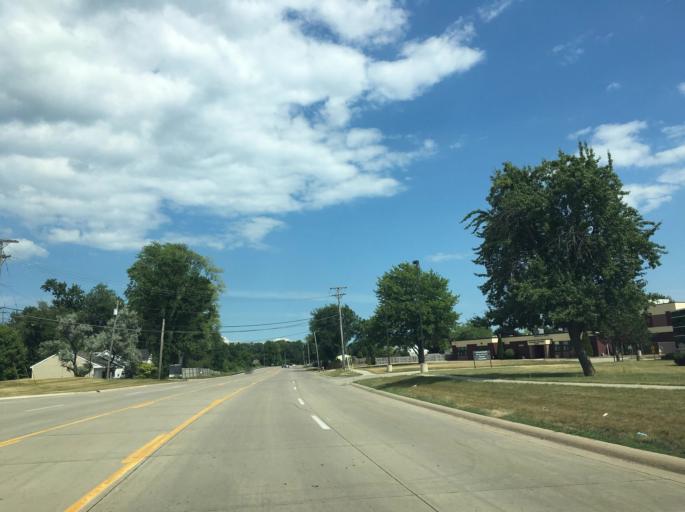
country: US
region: Michigan
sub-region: Macomb County
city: Clinton
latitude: 42.6101
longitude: -82.9281
